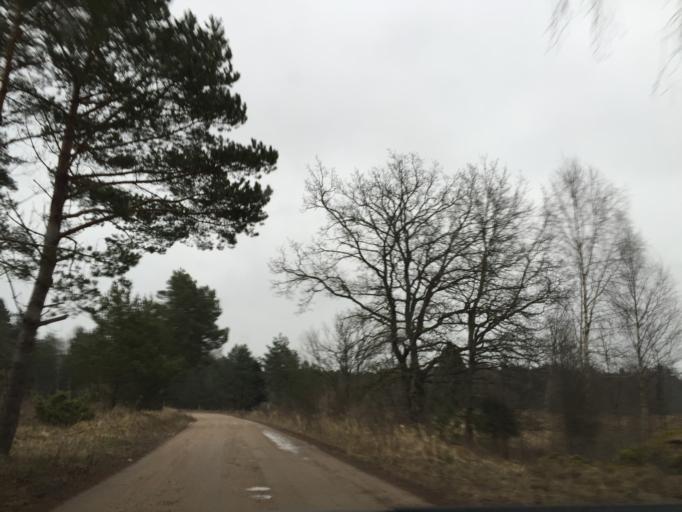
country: EE
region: Saare
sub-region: Kuressaare linn
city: Kuressaare
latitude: 58.4473
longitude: 22.2437
